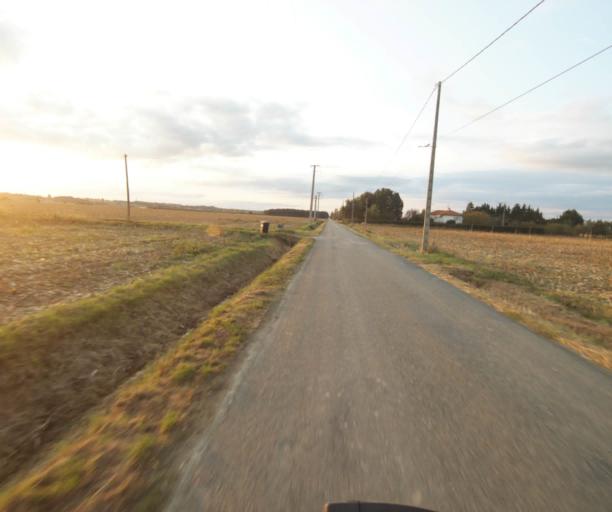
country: FR
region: Midi-Pyrenees
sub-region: Departement du Tarn-et-Garonne
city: Verdun-sur-Garonne
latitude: 43.8231
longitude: 1.2399
